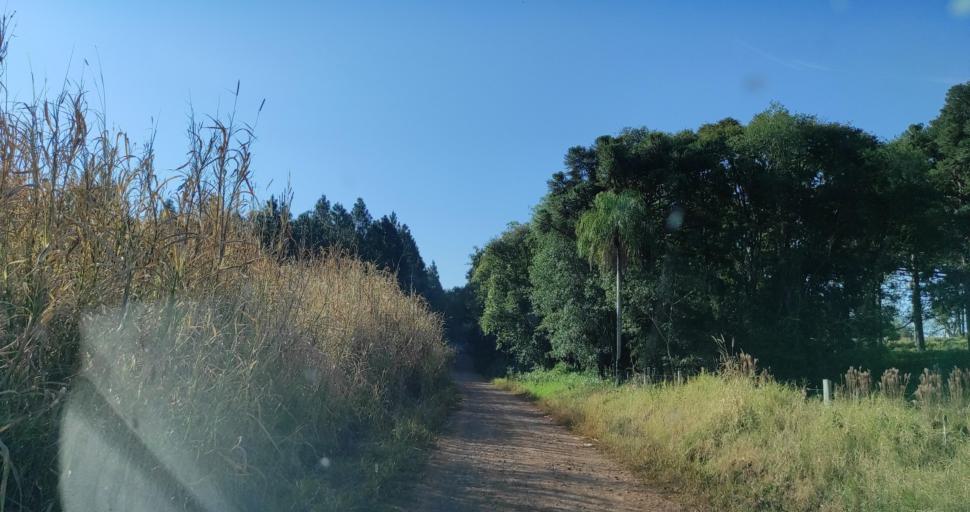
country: AR
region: Misiones
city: Capiovi
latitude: -26.8930
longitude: -55.1072
